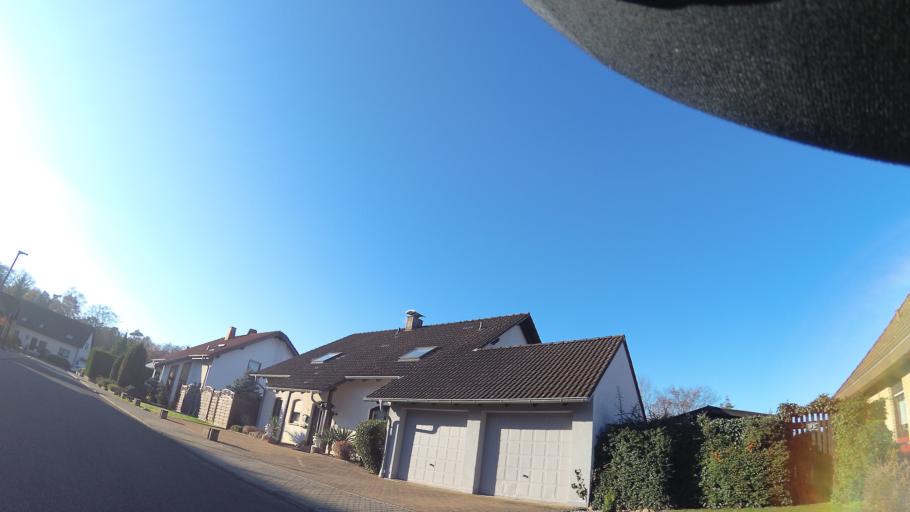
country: DE
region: Saarland
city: Schwalbach
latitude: 49.2957
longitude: 6.8145
